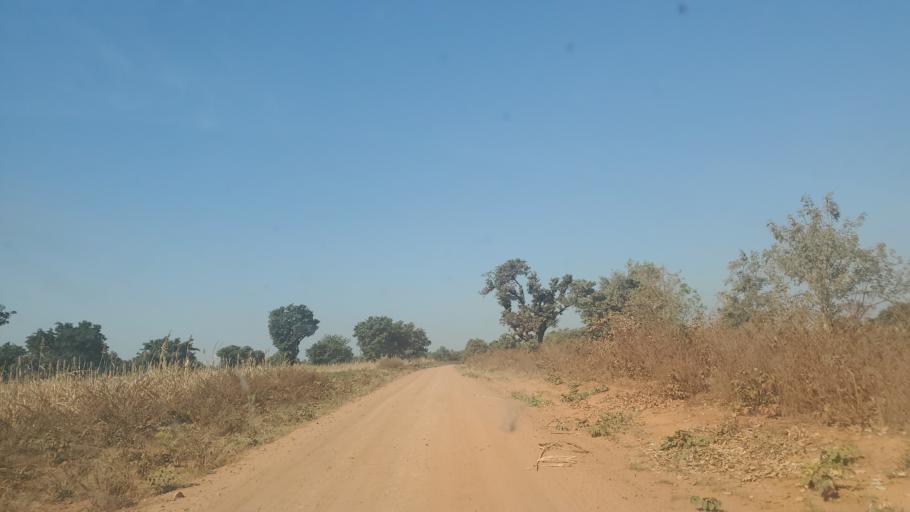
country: NG
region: Niger
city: Badeggi
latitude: 9.1197
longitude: 6.1927
